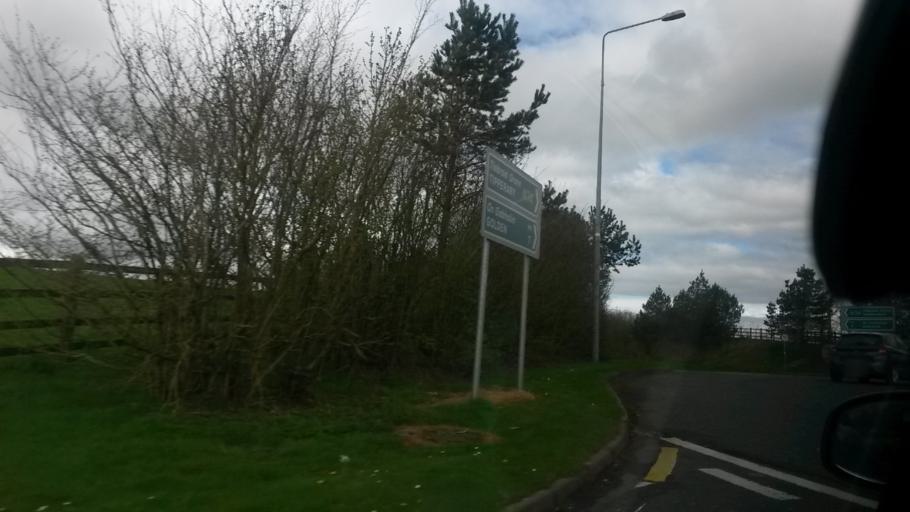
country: IE
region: Munster
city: Cashel
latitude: 52.5030
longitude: -7.8904
